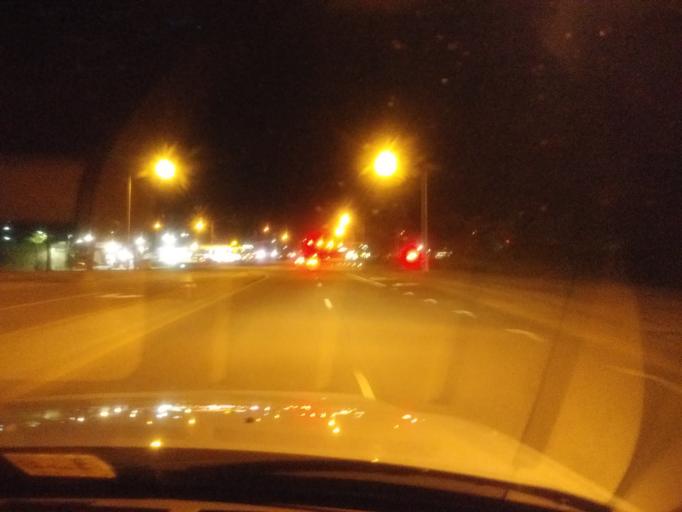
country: US
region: Virginia
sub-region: City of Chesapeake
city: Chesapeake
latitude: 36.7819
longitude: -76.1929
